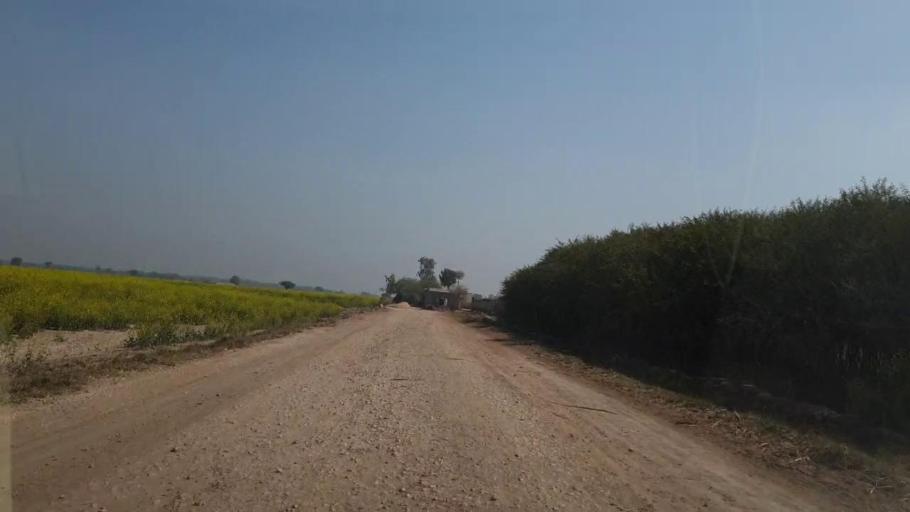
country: PK
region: Sindh
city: Matiari
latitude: 25.5341
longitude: 68.4670
